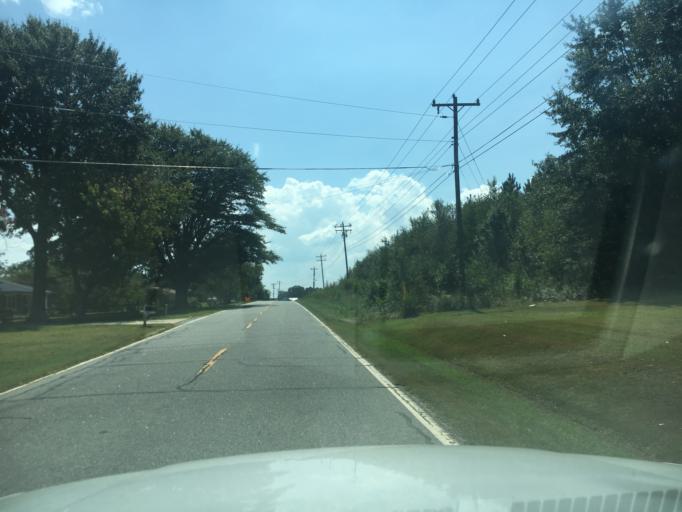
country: US
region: North Carolina
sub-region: Rutherford County
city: Forest City
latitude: 35.2413
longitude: -81.8472
